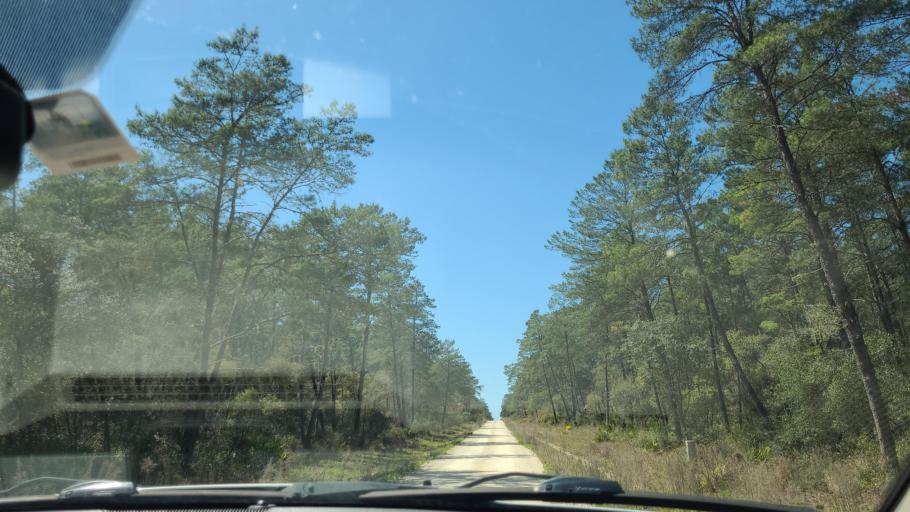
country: US
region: Florida
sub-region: Putnam County
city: Interlachen
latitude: 29.4284
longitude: -81.8773
